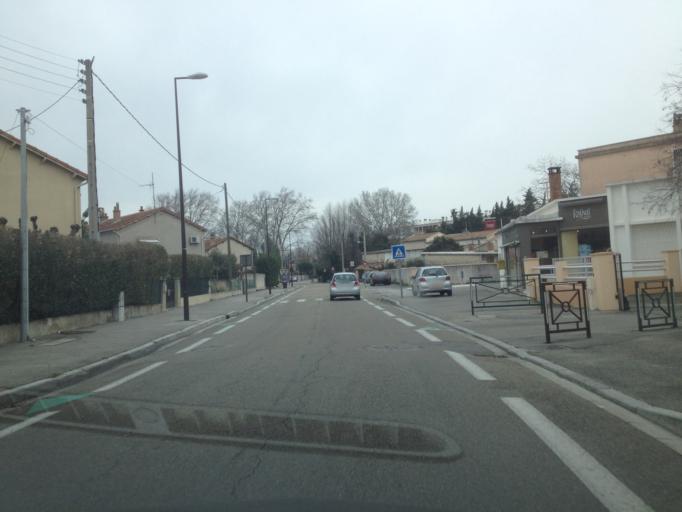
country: FR
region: Provence-Alpes-Cote d'Azur
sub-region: Departement du Vaucluse
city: Avignon
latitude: 43.9334
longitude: 4.8179
